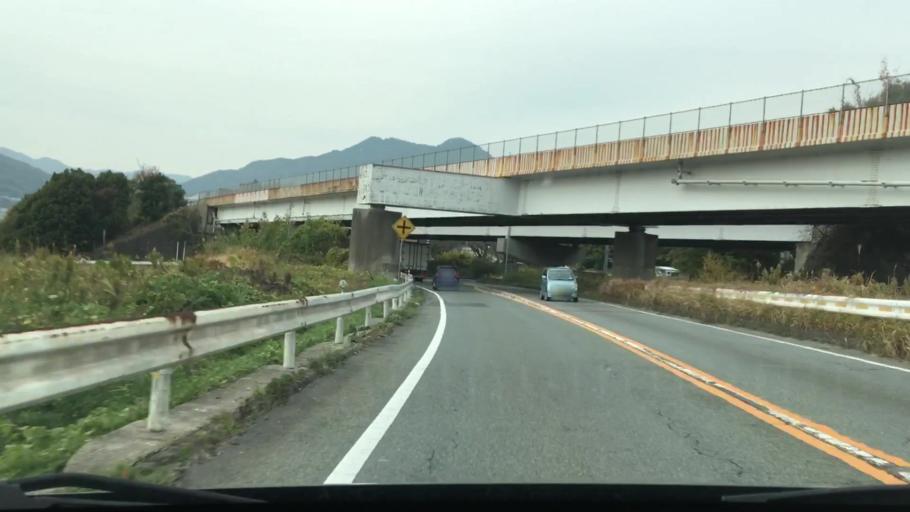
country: JP
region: Yamaguchi
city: Hofu
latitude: 34.0576
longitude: 131.6152
